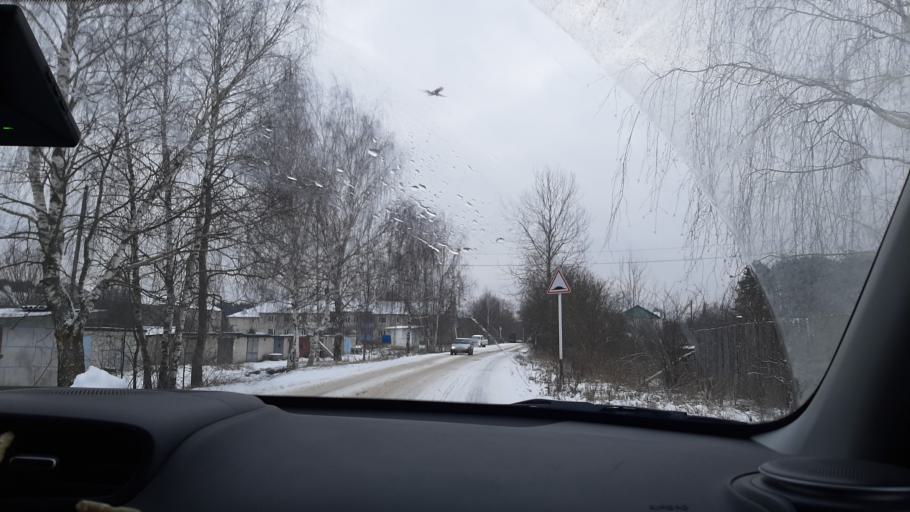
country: RU
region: Ivanovo
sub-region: Gorod Ivanovo
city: Ivanovo
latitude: 56.9276
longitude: 40.9817
